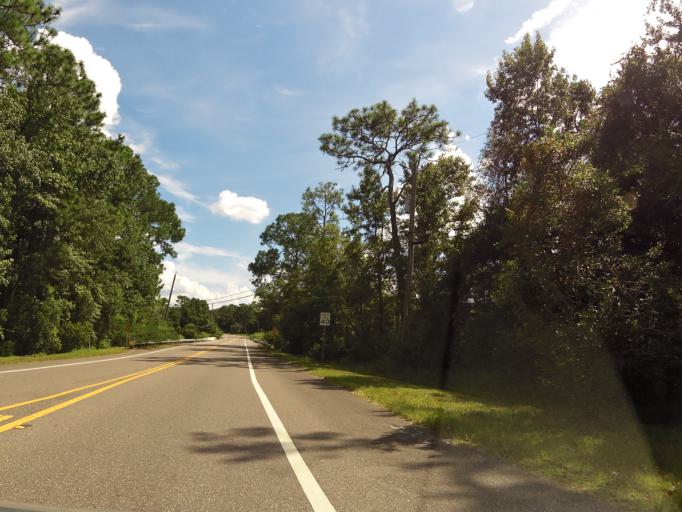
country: US
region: Florida
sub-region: Duval County
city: Jacksonville
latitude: 30.4301
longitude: -81.5803
